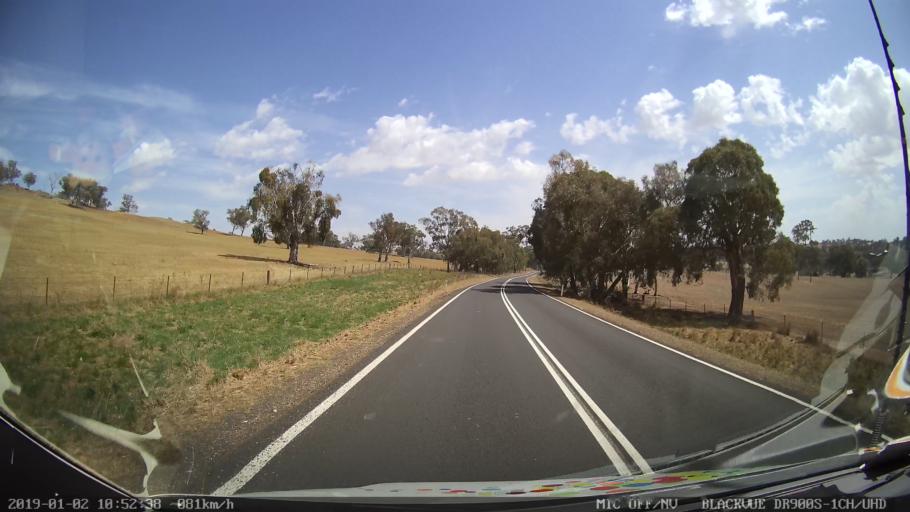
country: AU
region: New South Wales
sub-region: Cootamundra
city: Cootamundra
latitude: -34.6868
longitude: 148.2716
